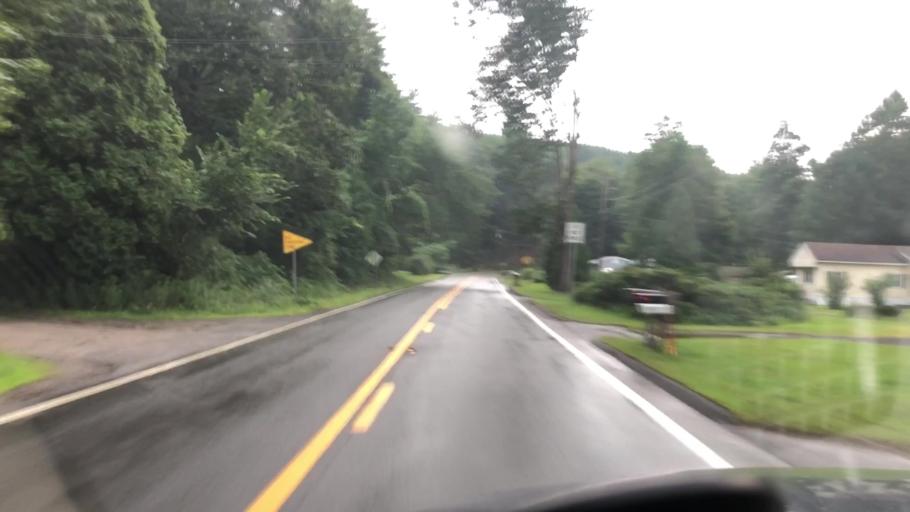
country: US
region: Massachusetts
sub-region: Hampshire County
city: Westhampton
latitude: 42.2622
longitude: -72.8644
